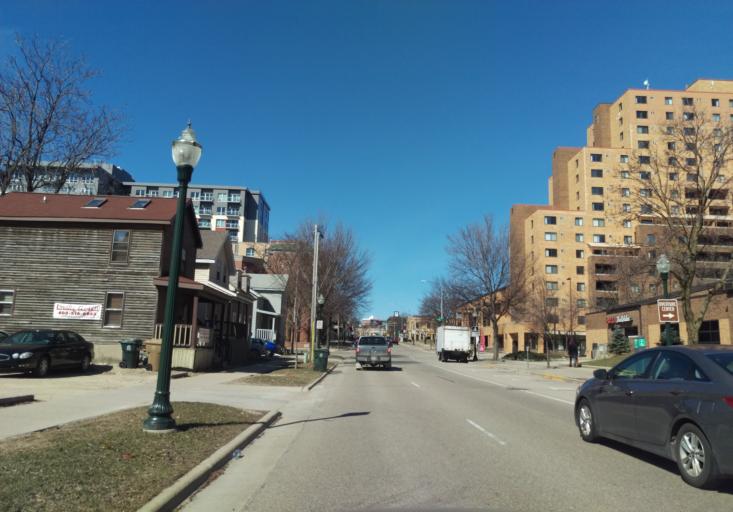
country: US
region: Wisconsin
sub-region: Dane County
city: Madison
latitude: 43.0724
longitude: -89.3903
